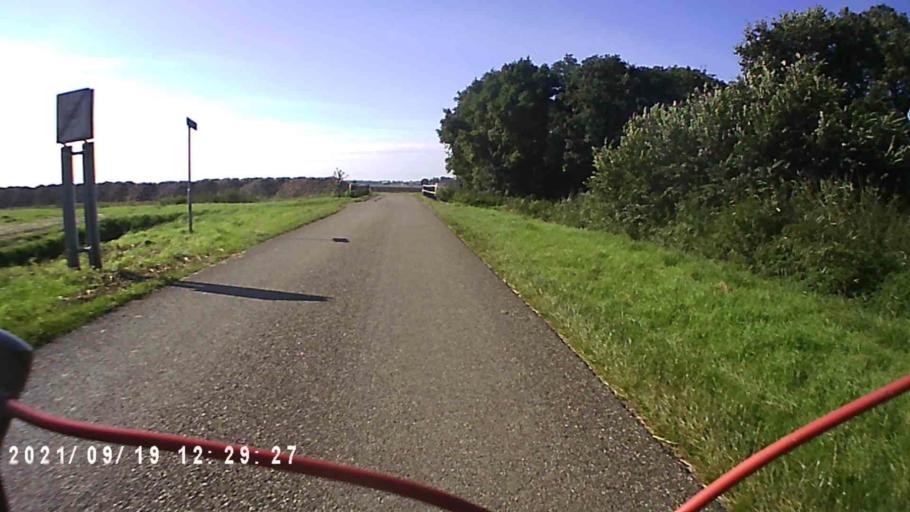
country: NL
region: Groningen
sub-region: Gemeente Slochteren
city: Slochteren
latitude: 53.2241
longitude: 6.8923
